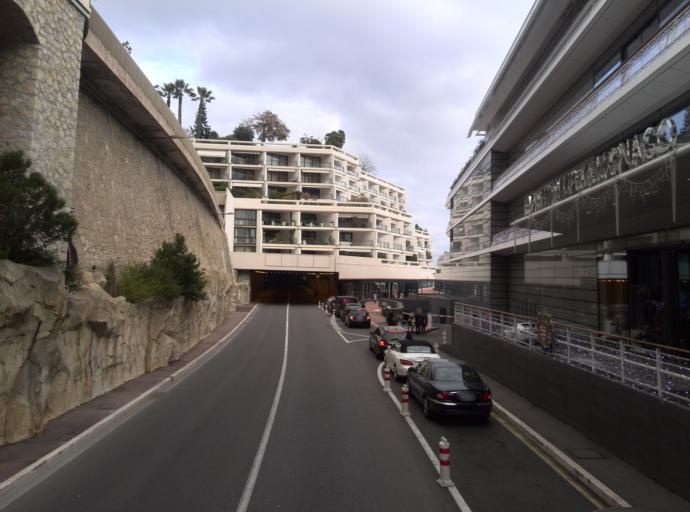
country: MC
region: Commune de Monaco
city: Monte-Carlo
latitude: 43.7374
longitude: 7.4269
